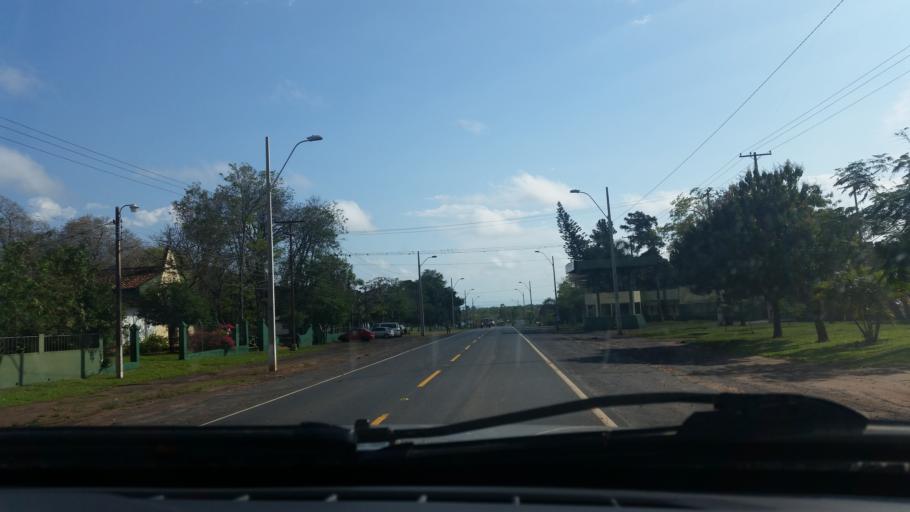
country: PY
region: Presidente Hayes
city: Benjamin Aceval
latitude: -24.9638
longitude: -57.5484
